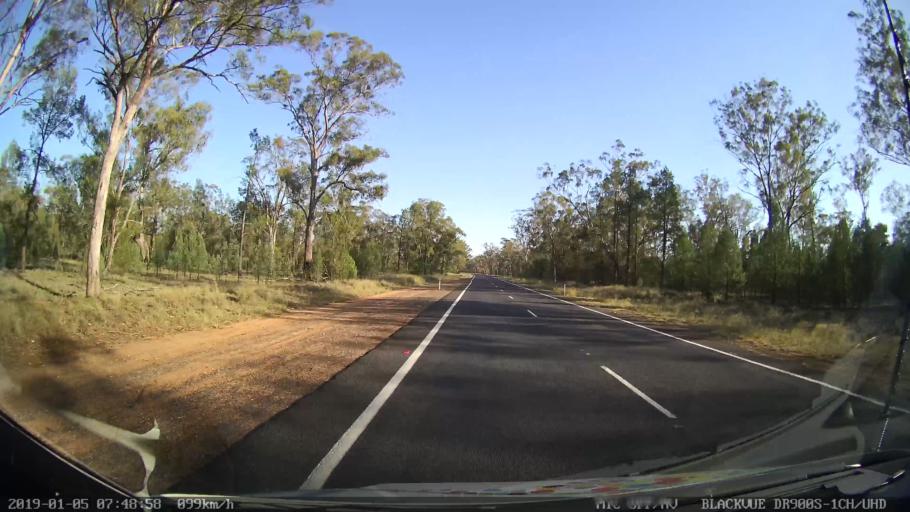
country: AU
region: New South Wales
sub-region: Gilgandra
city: Gilgandra
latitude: -31.8086
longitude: 148.6364
